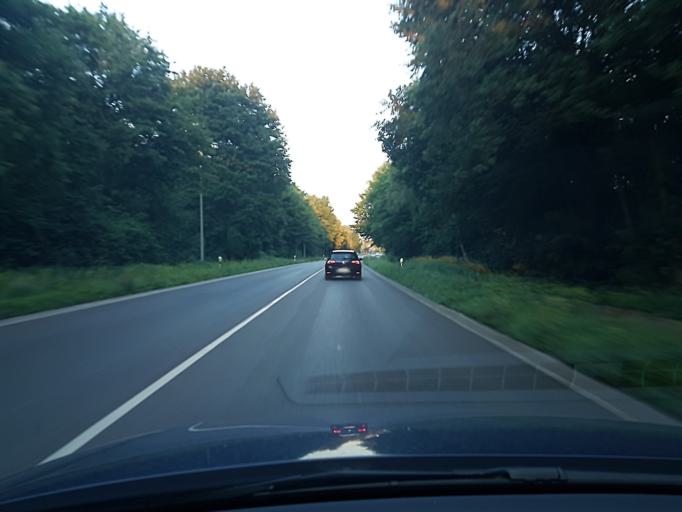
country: DE
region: North Rhine-Westphalia
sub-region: Regierungsbezirk Dusseldorf
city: Erkrath
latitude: 51.1967
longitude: 6.9051
